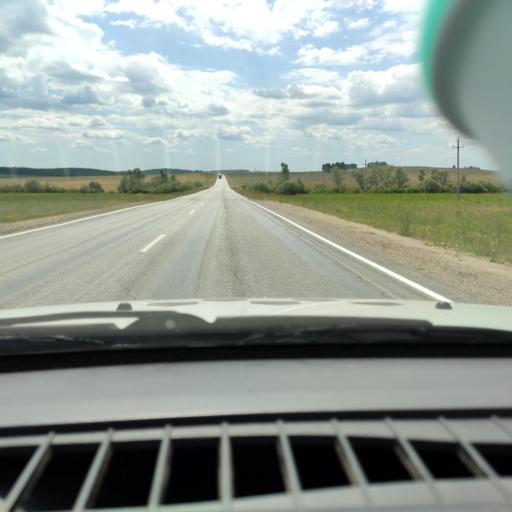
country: RU
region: Bashkortostan
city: Duvan
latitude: 55.9431
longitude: 58.1982
